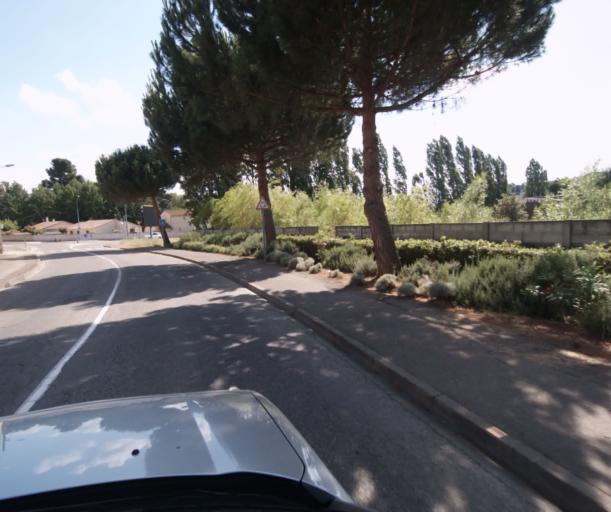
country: FR
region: Languedoc-Roussillon
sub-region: Departement de l'Aude
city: Limoux
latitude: 43.0603
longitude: 2.2214
